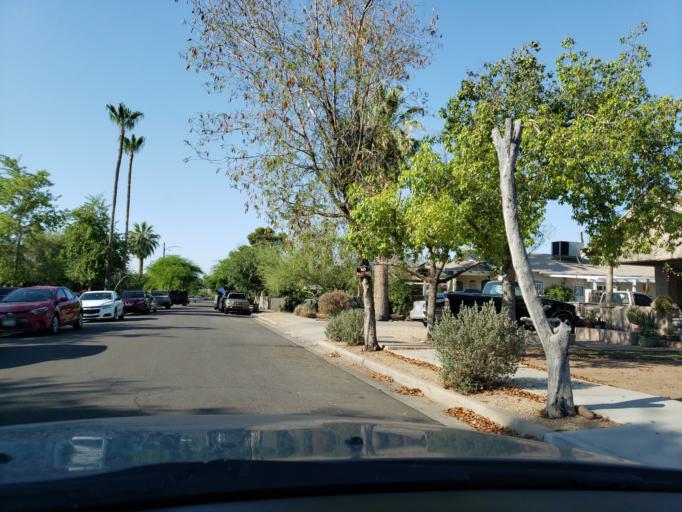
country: US
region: Arizona
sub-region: Maricopa County
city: Phoenix
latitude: 33.4729
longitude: -112.0640
